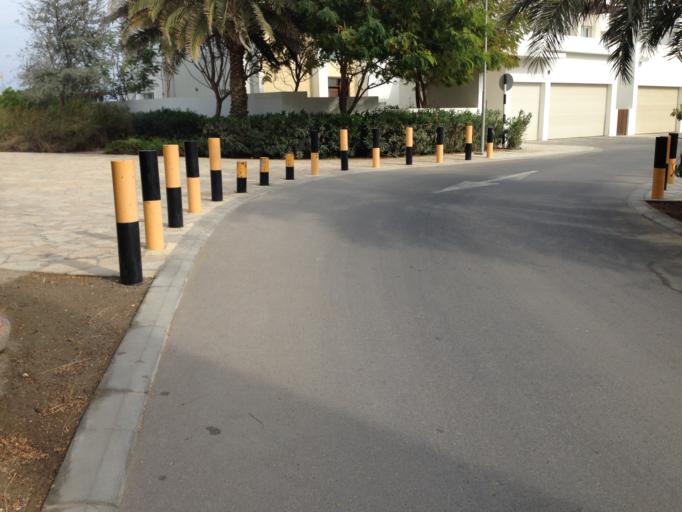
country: OM
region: Muhafazat Masqat
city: As Sib al Jadidah
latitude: 23.6266
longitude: 58.2733
